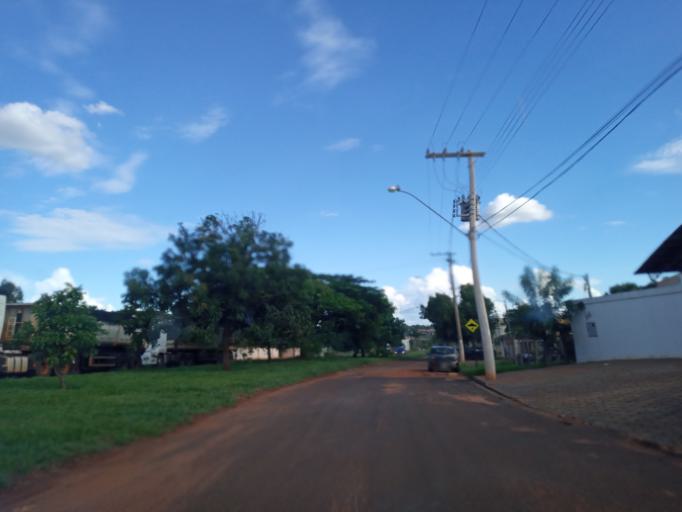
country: BR
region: Minas Gerais
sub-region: Ituiutaba
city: Ituiutaba
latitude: -18.9637
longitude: -49.4907
